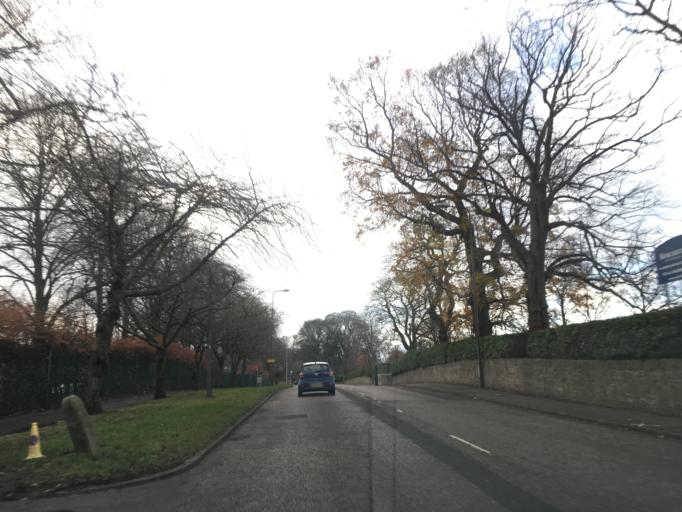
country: GB
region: Scotland
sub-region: Edinburgh
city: Colinton
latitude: 55.9123
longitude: -3.2462
